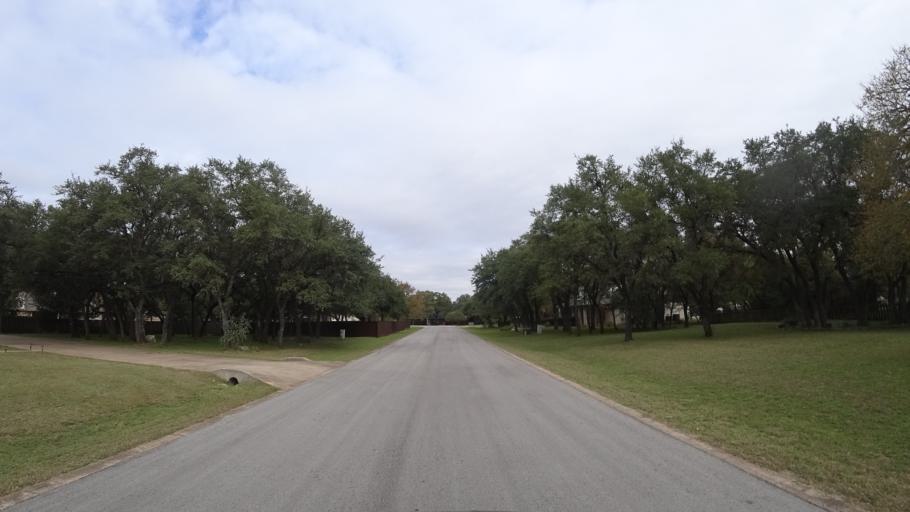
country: US
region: Texas
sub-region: Travis County
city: Shady Hollow
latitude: 30.1414
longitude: -97.8814
